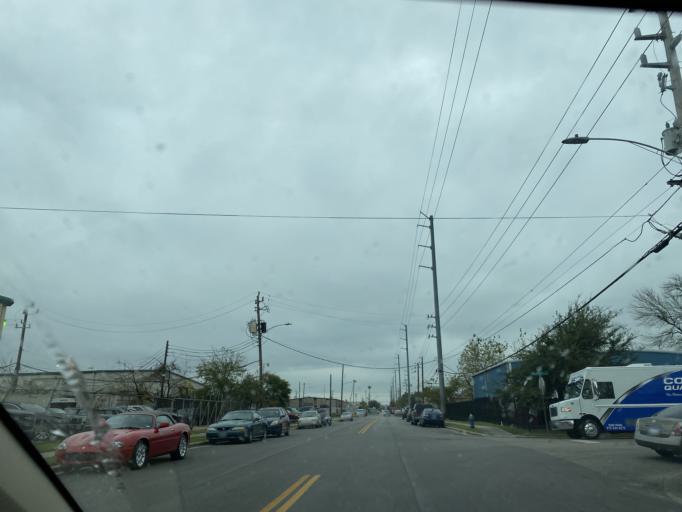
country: US
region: Texas
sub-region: Harris County
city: Piney Point Village
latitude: 29.7255
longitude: -95.5195
